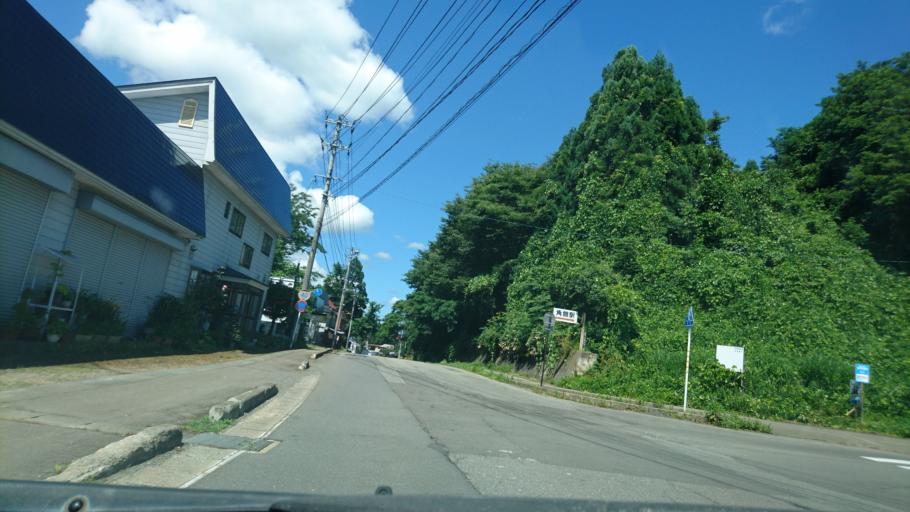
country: JP
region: Akita
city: Kakunodatemachi
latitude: 39.5884
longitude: 140.5671
